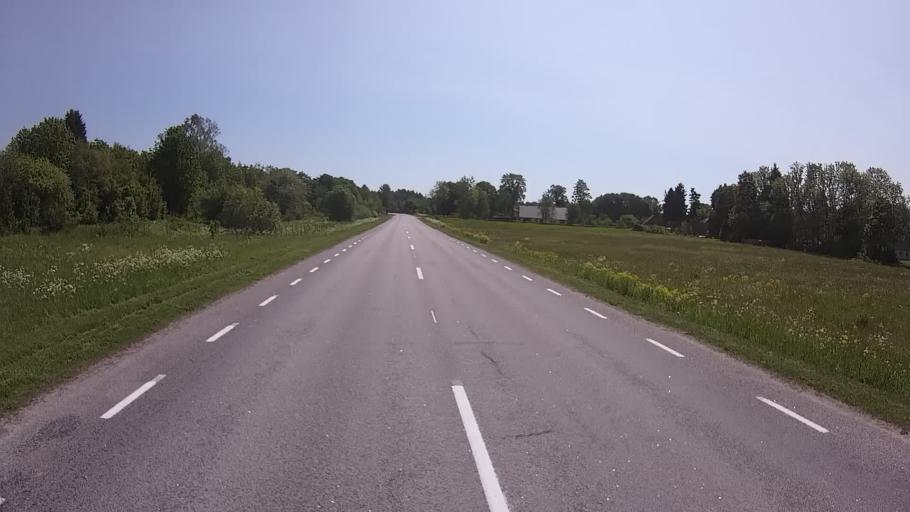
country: EE
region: Saare
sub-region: Kuressaare linn
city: Kuressaare
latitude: 58.3057
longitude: 22.2530
